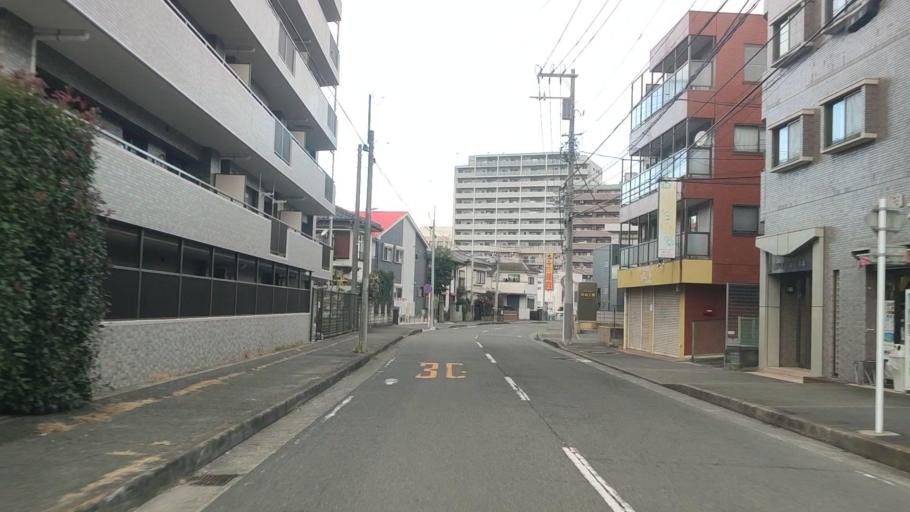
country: JP
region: Kanagawa
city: Minami-rinkan
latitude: 35.4661
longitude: 139.4639
